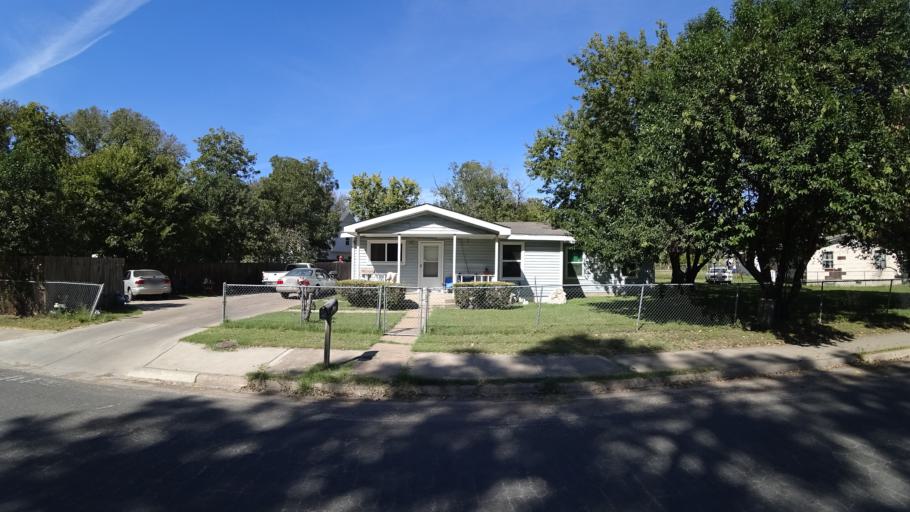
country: US
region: Texas
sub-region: Travis County
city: Austin
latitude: 30.2676
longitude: -97.6842
